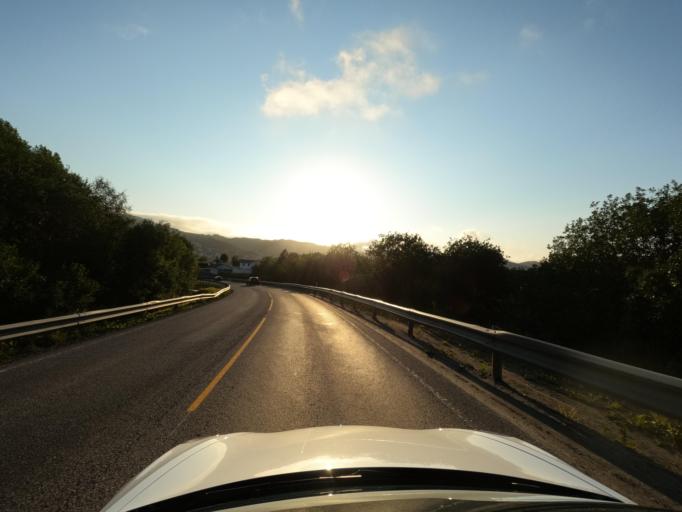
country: NO
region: Troms
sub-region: Harstad
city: Harstad
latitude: 68.7835
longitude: 16.5611
